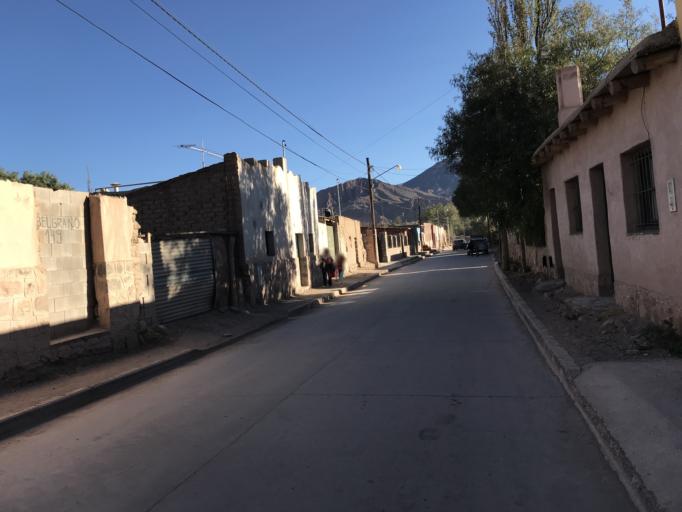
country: AR
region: Jujuy
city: Maimara
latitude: -23.5773
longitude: -65.4001
